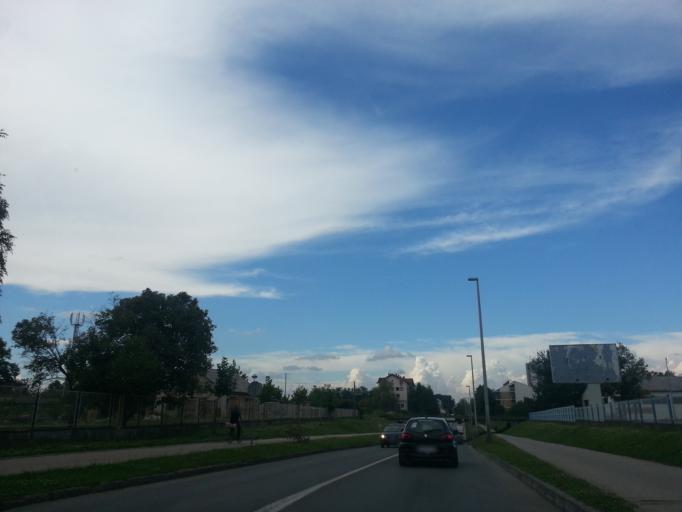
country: BA
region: Brcko
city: Brcko
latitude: 44.8642
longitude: 18.8113
